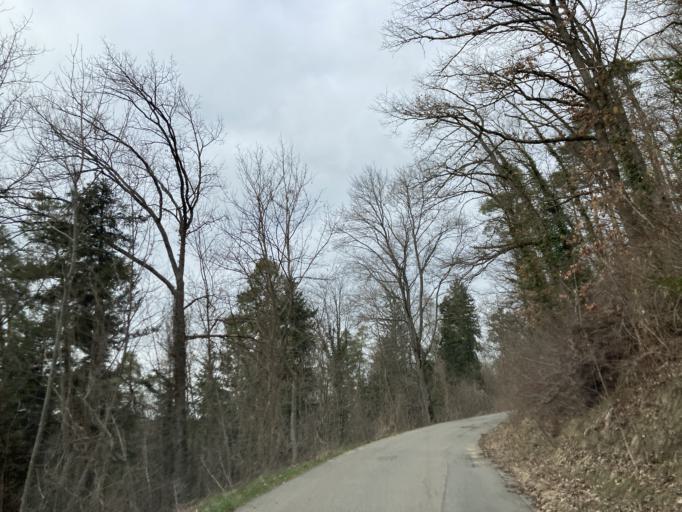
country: DE
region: Baden-Wuerttemberg
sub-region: Tuebingen Region
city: Rottenburg
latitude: 48.4563
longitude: 8.9036
